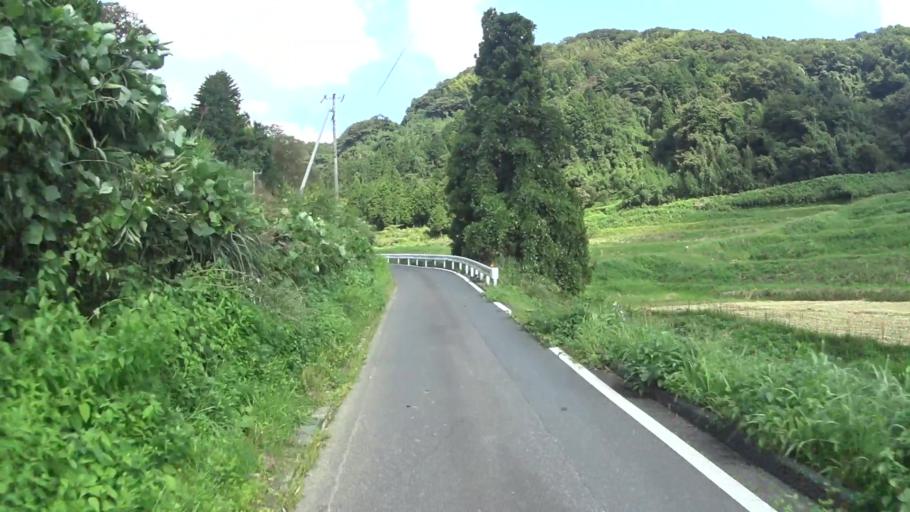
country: JP
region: Kyoto
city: Miyazu
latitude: 35.6559
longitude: 135.2354
